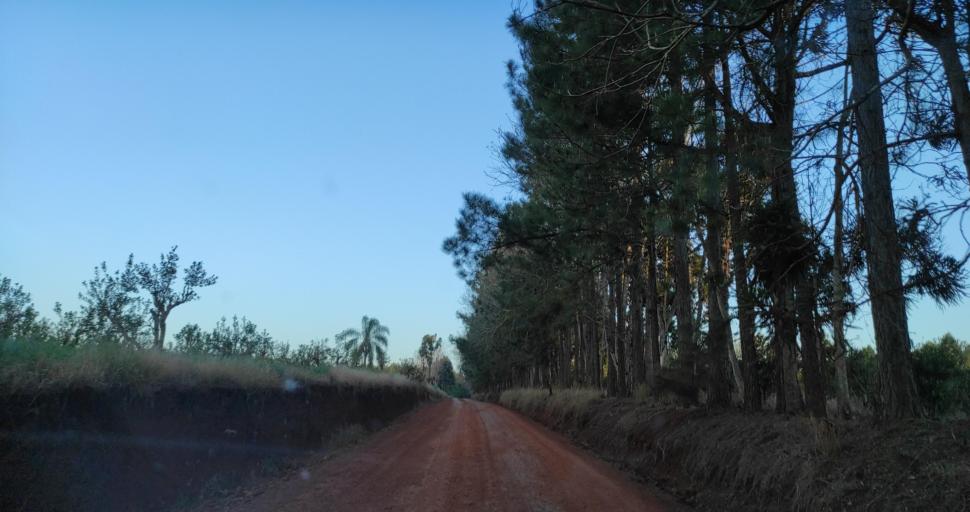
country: AR
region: Misiones
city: Capiovi
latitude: -26.8743
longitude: -55.0972
